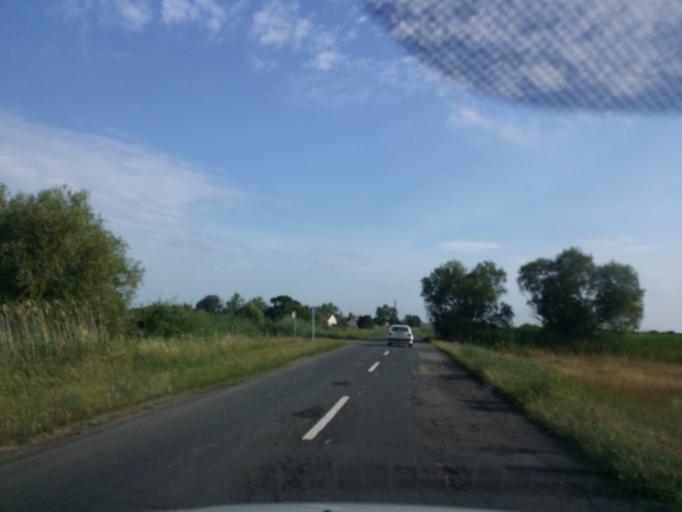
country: HU
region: Hajdu-Bihar
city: Hortobagy
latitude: 47.6018
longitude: 21.0761
